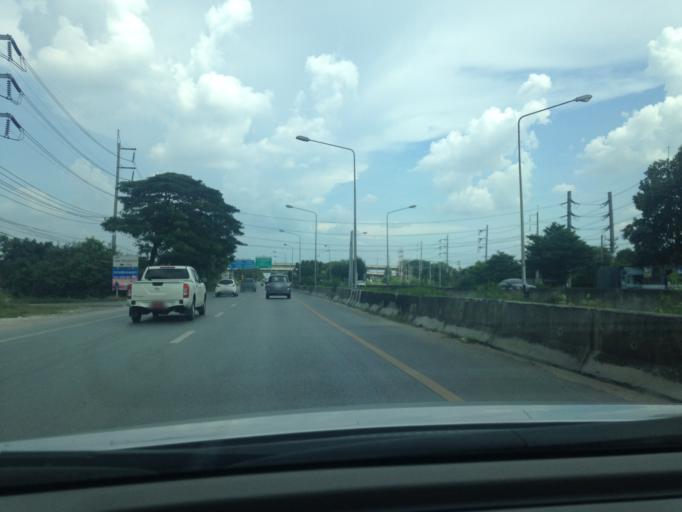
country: TH
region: Pathum Thani
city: Sam Khok
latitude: 14.0662
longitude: 100.5744
